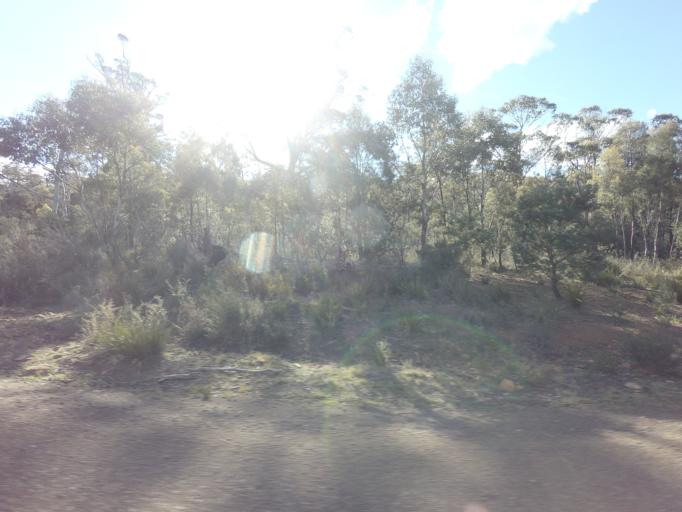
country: AU
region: Tasmania
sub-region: Break O'Day
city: St Helens
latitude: -41.8435
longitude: 148.0132
